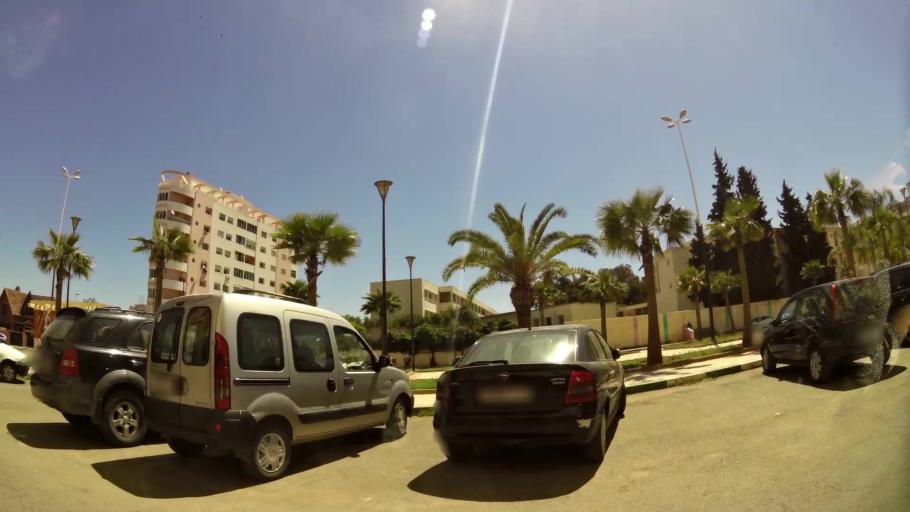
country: MA
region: Meknes-Tafilalet
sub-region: Meknes
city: Meknes
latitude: 33.9003
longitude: -5.5325
